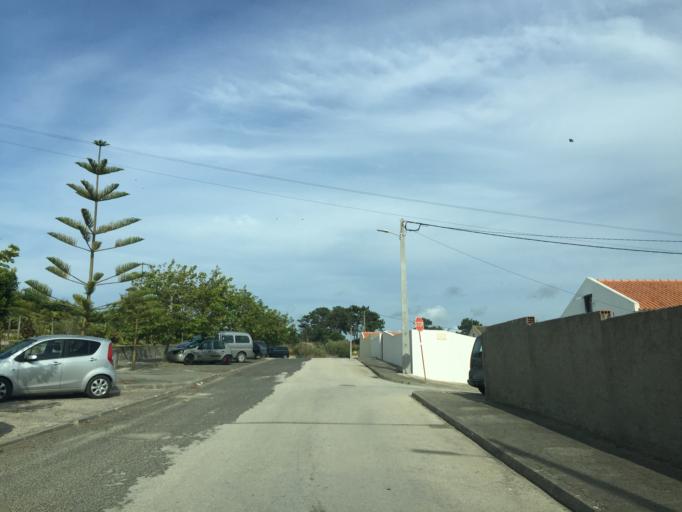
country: PT
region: Leiria
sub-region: Peniche
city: Atouguia da Baleia
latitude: 39.3639
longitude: -9.3113
